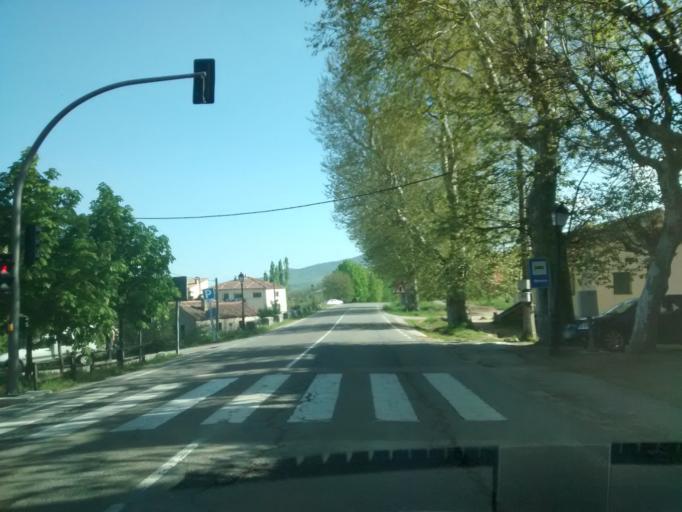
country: ES
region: Castille and Leon
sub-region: Provincia de Segovia
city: San Ildefonso
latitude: 40.8752
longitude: -4.0208
